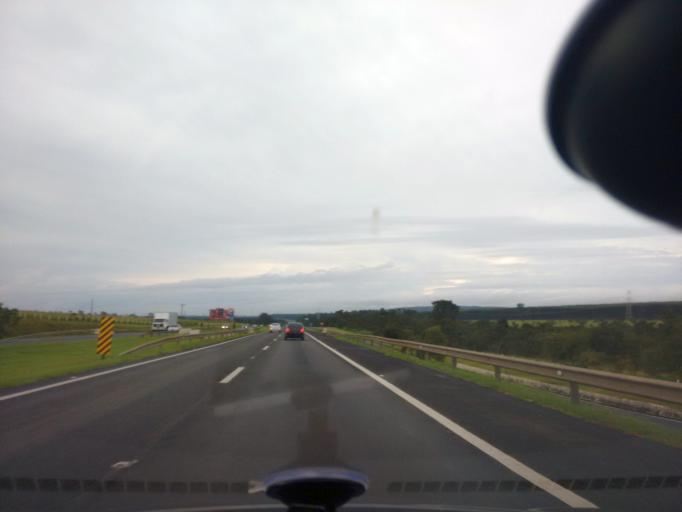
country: BR
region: Sao Paulo
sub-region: Itirapina
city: Itirapina
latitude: -22.1711
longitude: -47.7862
